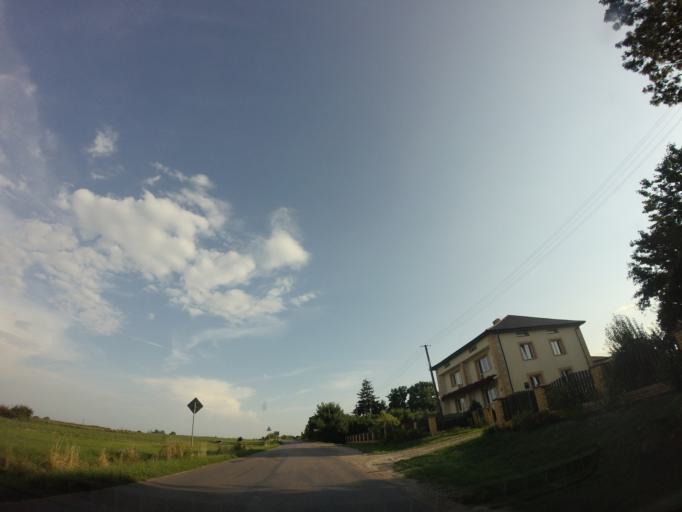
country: PL
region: Lublin Voivodeship
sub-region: Powiat lubartowski
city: Abramow
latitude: 51.4573
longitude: 22.2776
